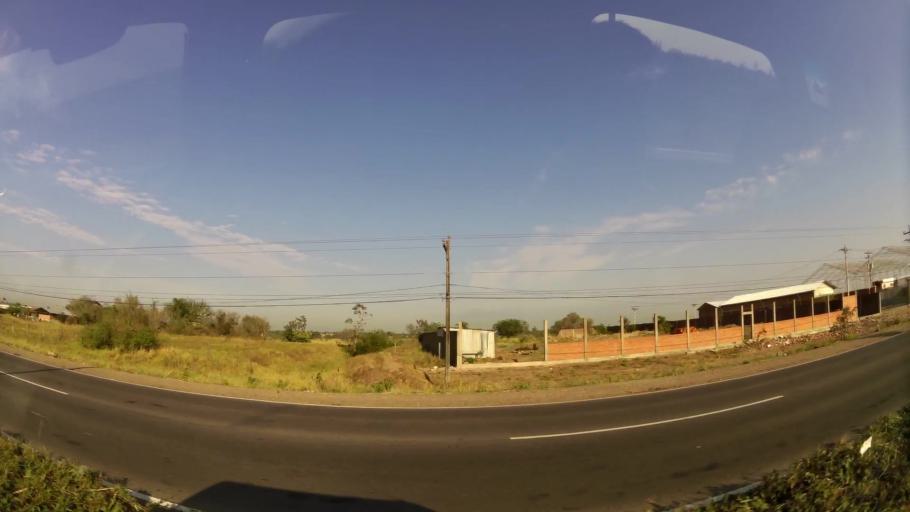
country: BO
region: Santa Cruz
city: La Belgica
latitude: -17.6406
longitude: -63.1576
